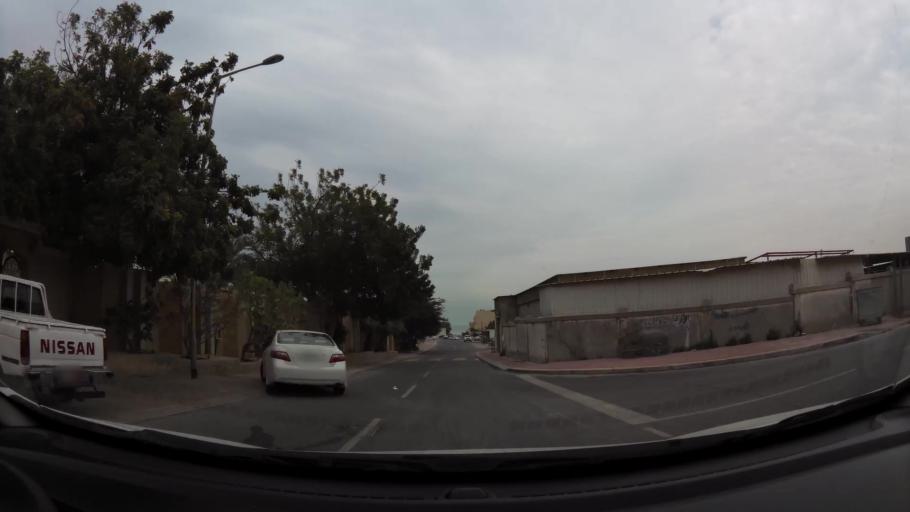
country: BH
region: Northern
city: Ar Rifa'
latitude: 26.0594
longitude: 50.6151
